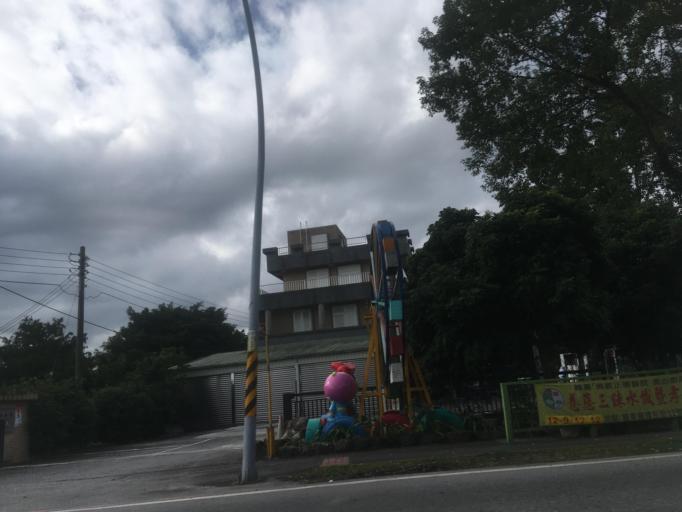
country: TW
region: Taiwan
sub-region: Yilan
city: Yilan
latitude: 24.6892
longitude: 121.7358
